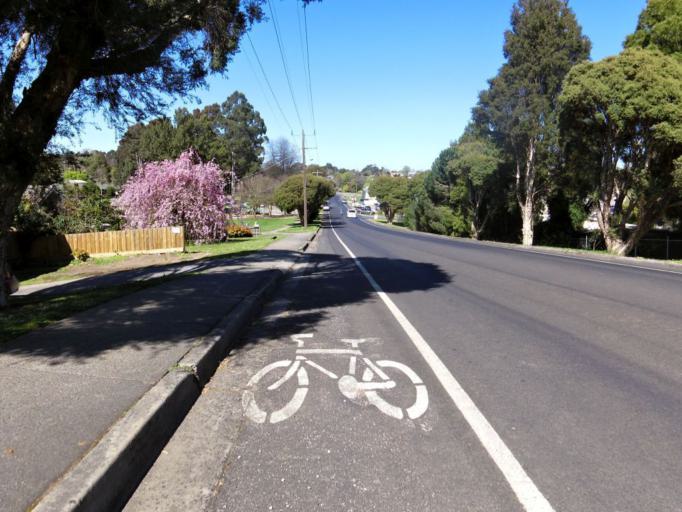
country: AU
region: Victoria
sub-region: Baw Baw
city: Warragul
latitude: -38.1567
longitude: 145.9232
